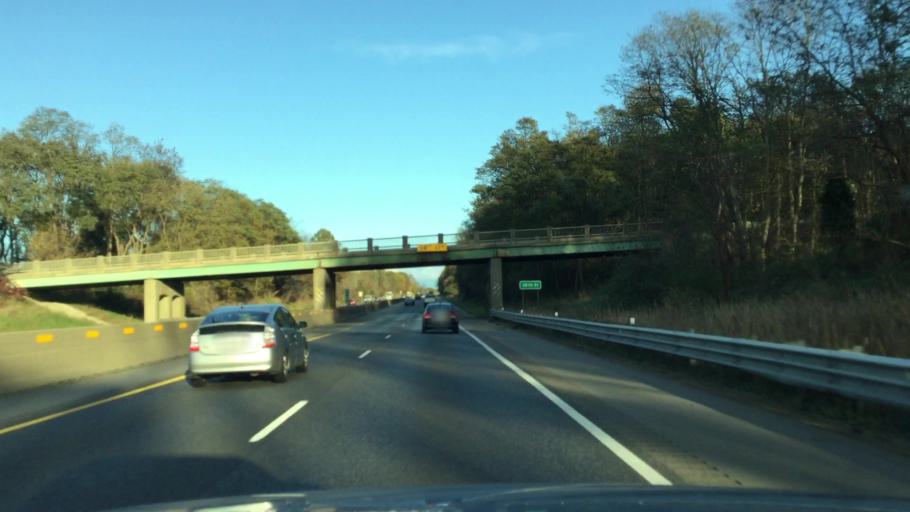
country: US
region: Michigan
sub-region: Kalamazoo County
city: Galesburg
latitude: 42.2783
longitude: -85.4013
